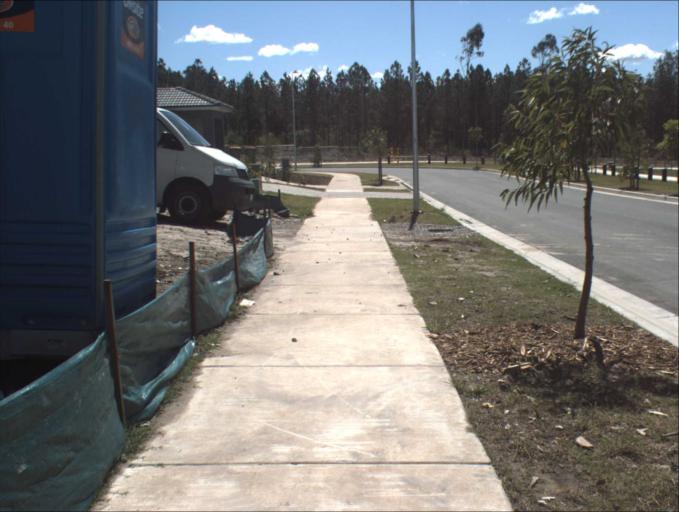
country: AU
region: Queensland
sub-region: Logan
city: Chambers Flat
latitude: -27.7968
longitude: 153.1084
